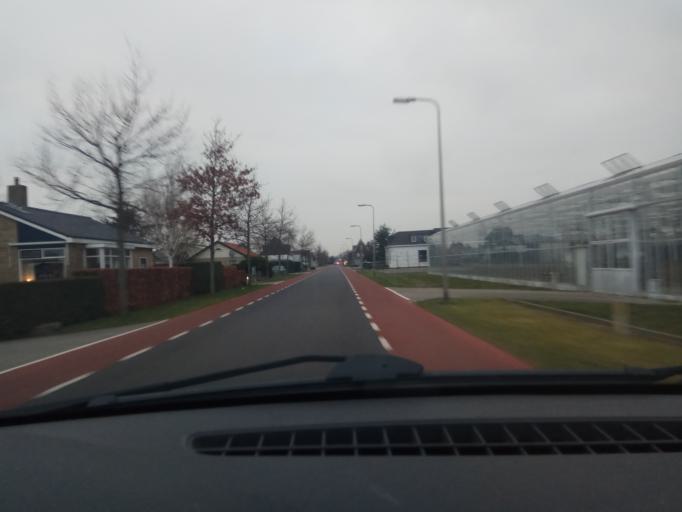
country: NL
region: South Holland
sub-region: Gemeente Westland
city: Maasdijk
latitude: 51.9518
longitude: 4.2173
